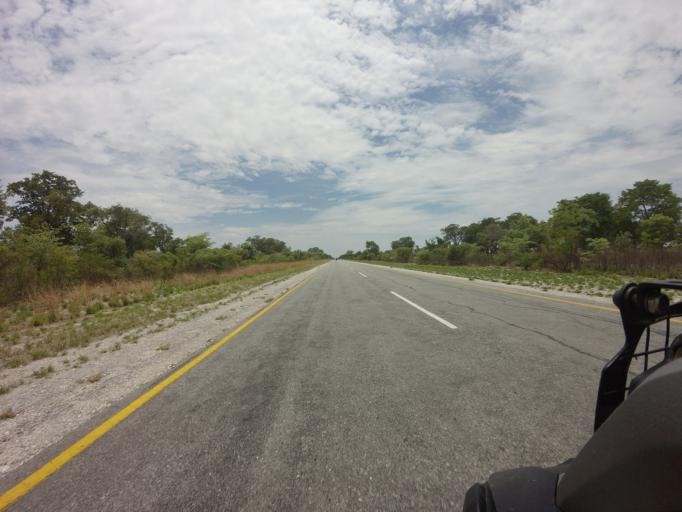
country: BW
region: North West
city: Shakawe
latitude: -18.0478
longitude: 22.0291
